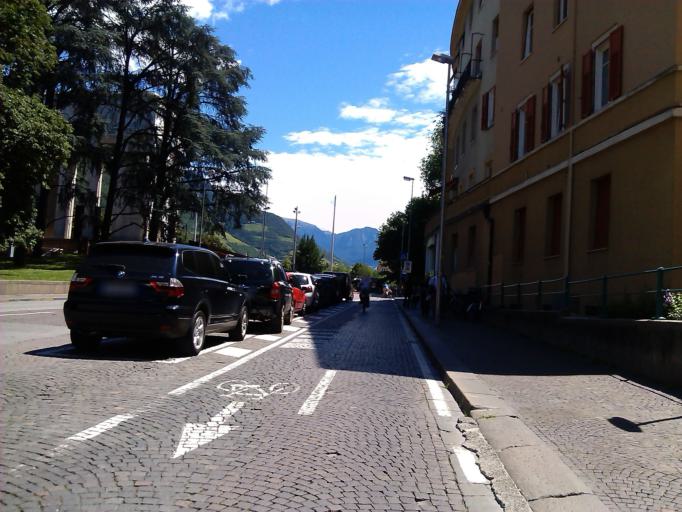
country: IT
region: Trentino-Alto Adige
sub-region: Bolzano
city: Bolzano
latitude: 46.5002
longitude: 11.3439
